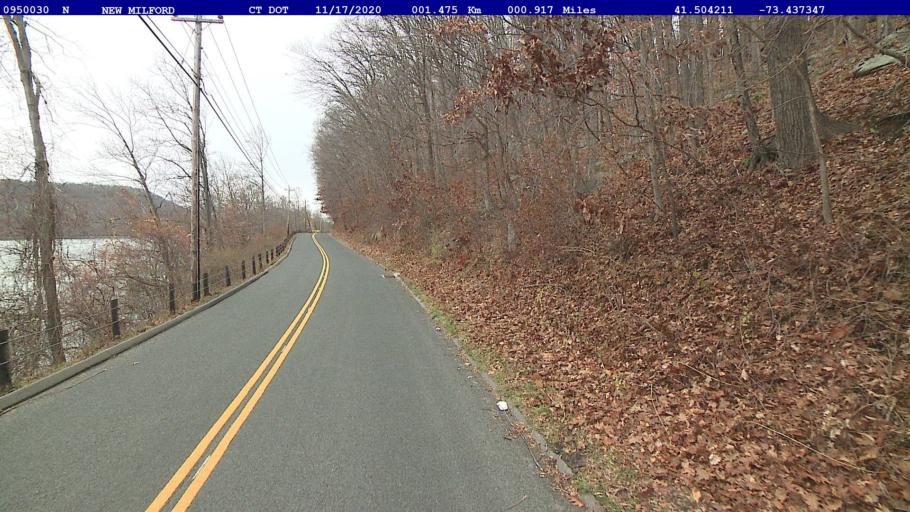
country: US
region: Connecticut
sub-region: Litchfield County
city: New Milford
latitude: 41.5042
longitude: -73.4373
